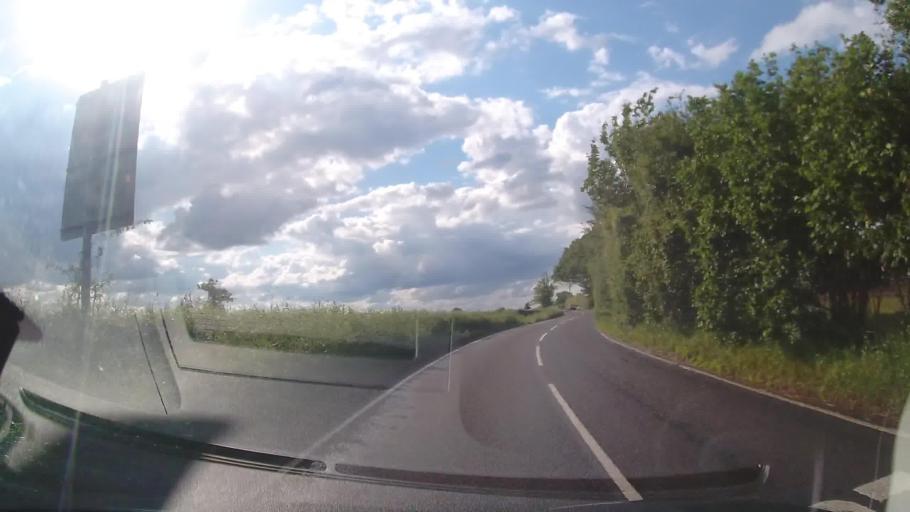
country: GB
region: England
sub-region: Shropshire
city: Harley
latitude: 52.6561
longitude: -2.6140
